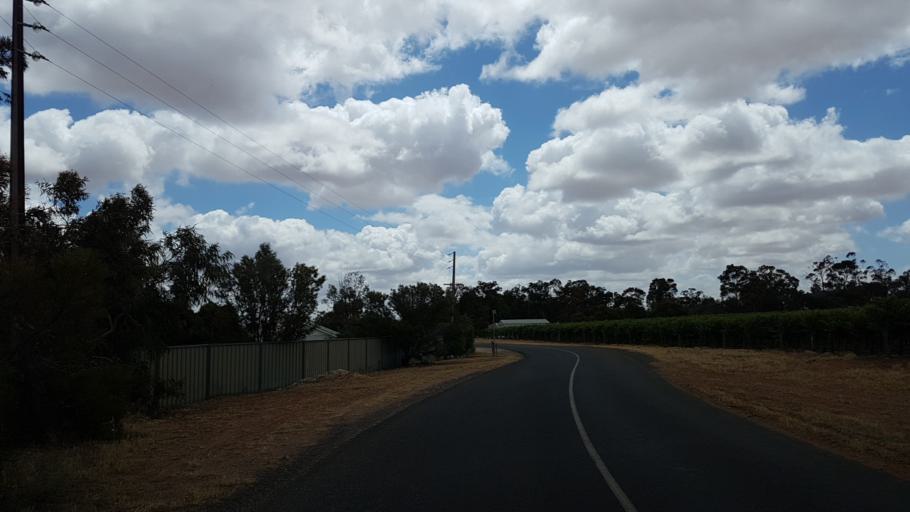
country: AU
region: South Australia
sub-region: Loxton Waikerie
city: Waikerie
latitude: -34.1728
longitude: 140.0308
